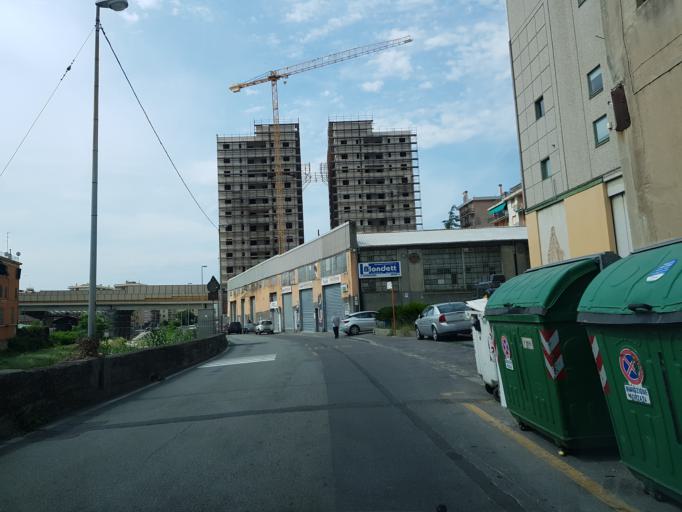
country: IT
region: Liguria
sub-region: Provincia di Genova
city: San Teodoro
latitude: 44.4317
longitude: 8.8544
